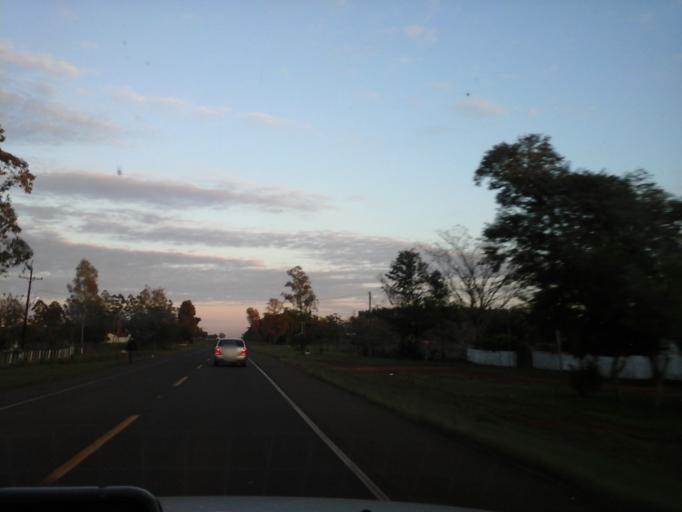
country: PY
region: Itapua
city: General Delgado
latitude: -27.0855
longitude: -56.5420
